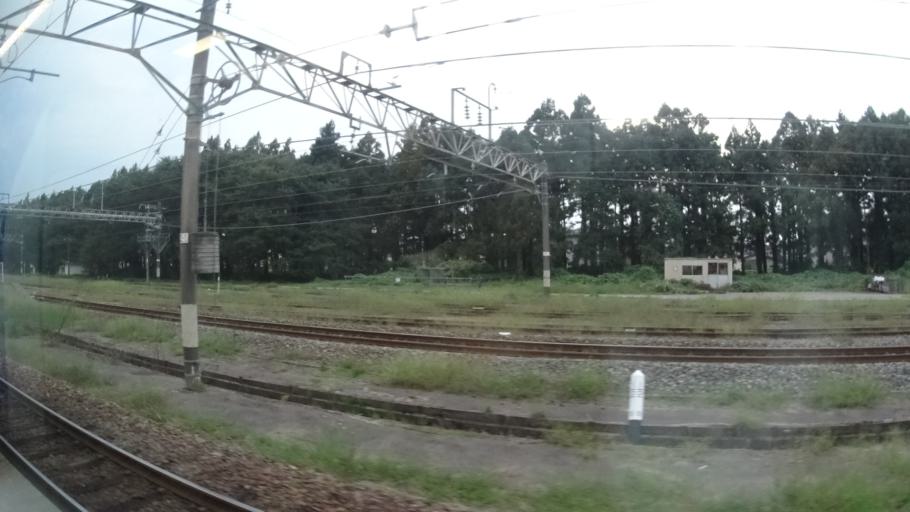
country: JP
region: Niigata
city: Murakami
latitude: 38.2214
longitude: 139.4634
